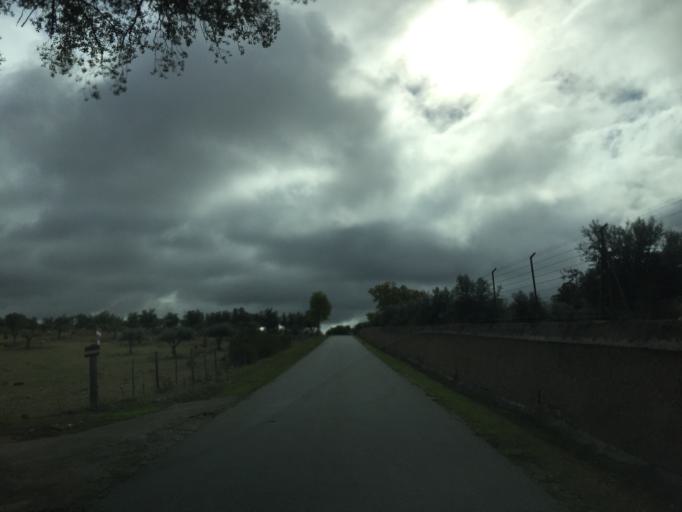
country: PT
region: Portalegre
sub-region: Alter do Chao
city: Alter do Chao
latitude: 39.2266
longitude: -7.6792
